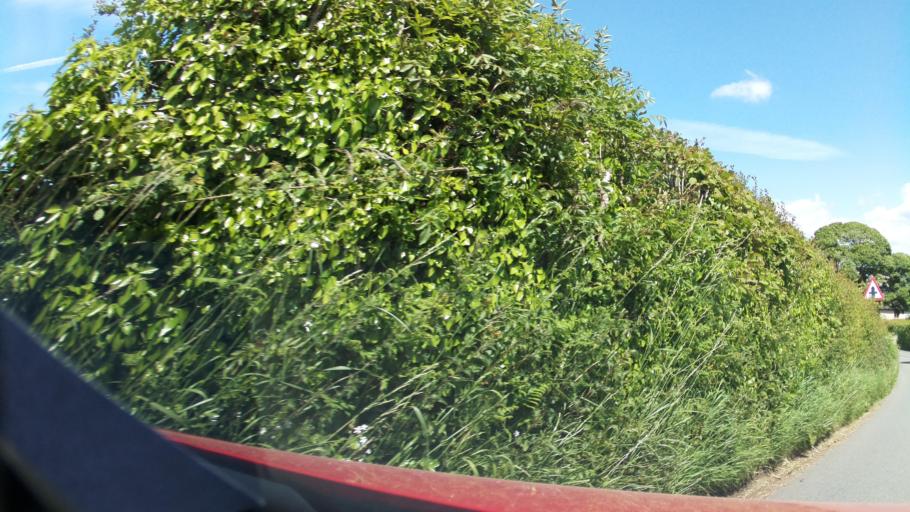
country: GB
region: Wales
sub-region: Monmouthshire
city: Mitchel Troy
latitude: 51.7224
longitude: -2.7597
